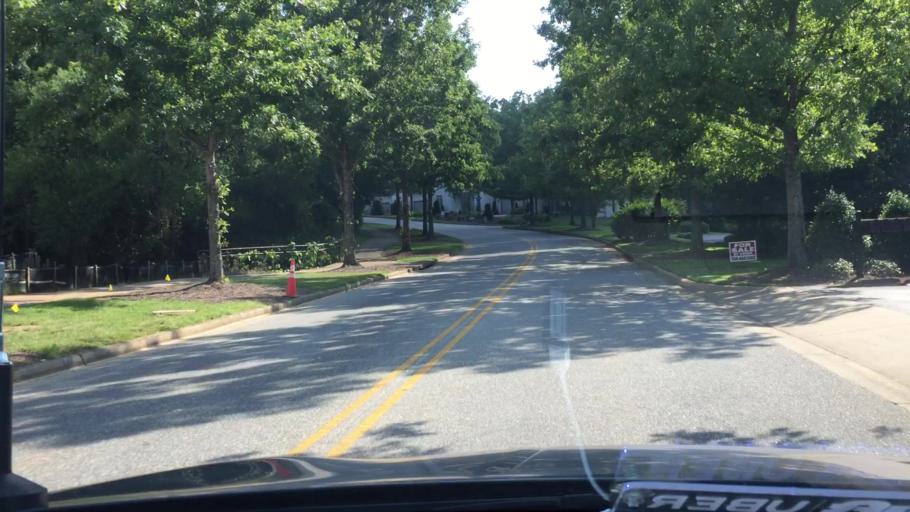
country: US
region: Alabama
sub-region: Lee County
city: Auburn
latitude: 32.5828
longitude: -85.4430
